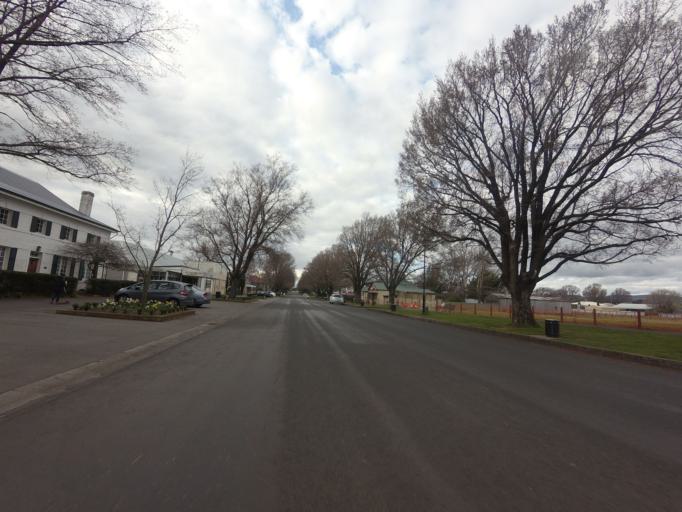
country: AU
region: Tasmania
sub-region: Northern Midlands
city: Evandale
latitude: -42.0303
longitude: 147.4923
